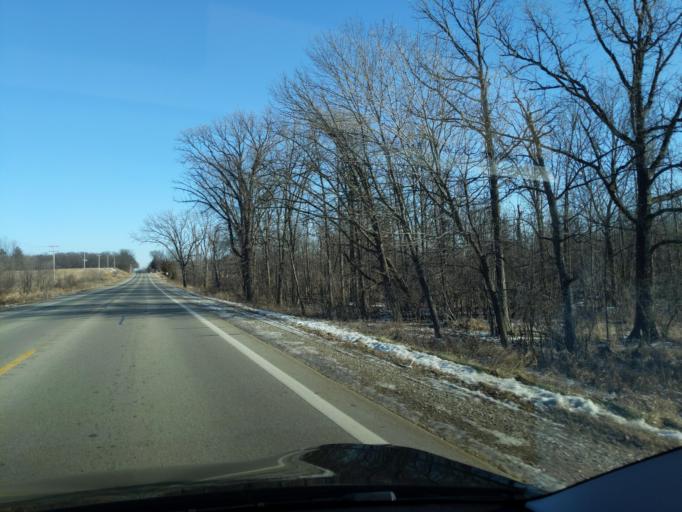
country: US
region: Michigan
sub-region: Ingham County
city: Stockbridge
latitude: 42.3944
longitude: -84.3029
